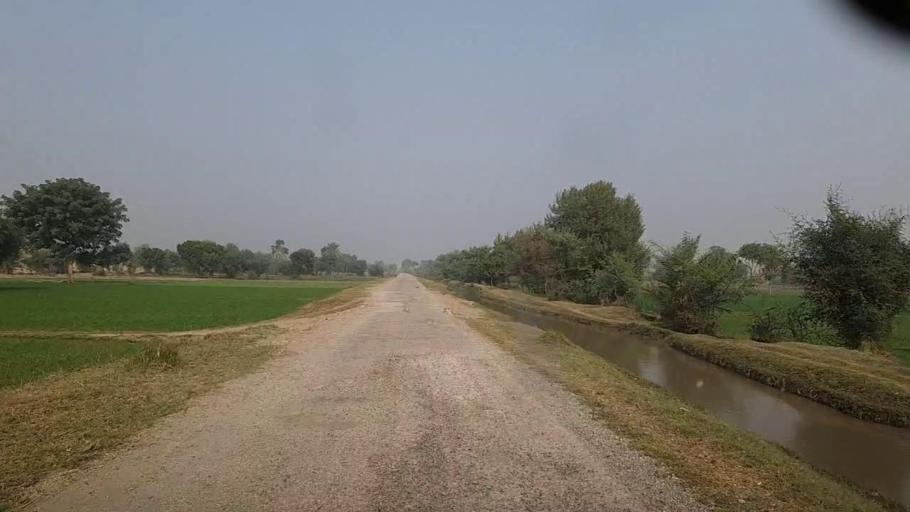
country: PK
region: Sindh
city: Bozdar
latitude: 27.0611
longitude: 68.6347
